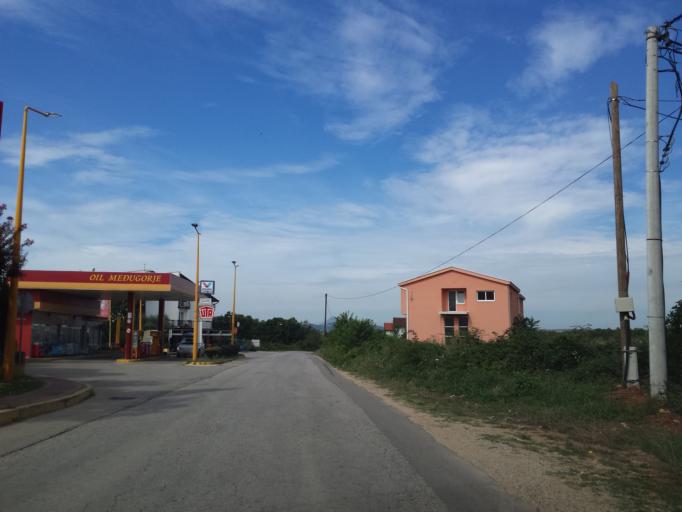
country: BA
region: Federation of Bosnia and Herzegovina
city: Citluk
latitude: 43.1975
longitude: 17.6692
